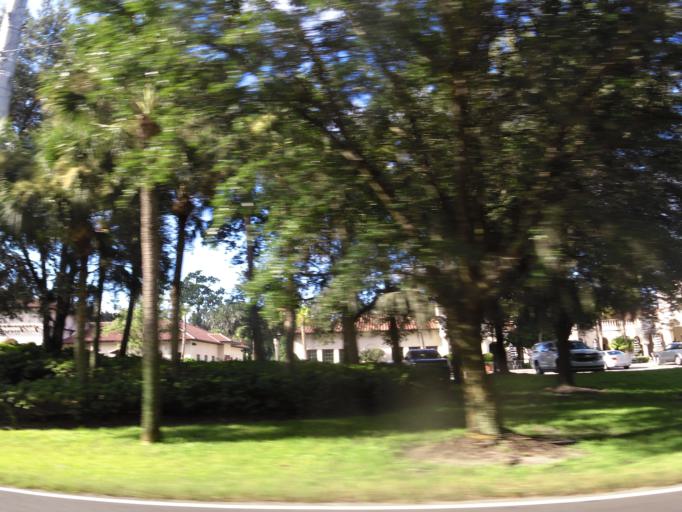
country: US
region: Georgia
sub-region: Glynn County
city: Saint Simons Island
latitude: 31.1833
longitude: -81.3749
